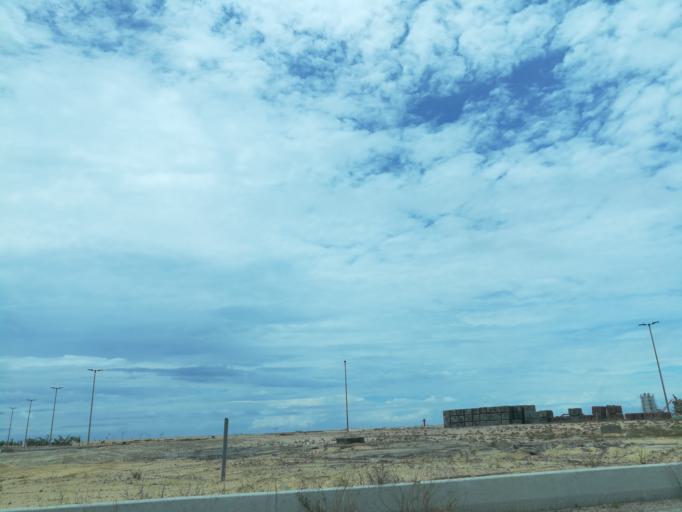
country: NG
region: Lagos
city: Ikoyi
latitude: 6.4124
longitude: 3.4259
